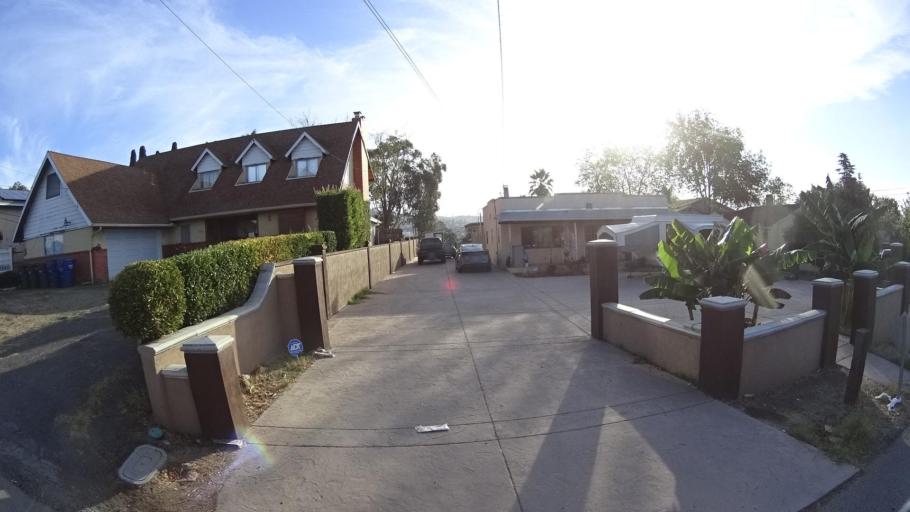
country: US
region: California
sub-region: San Diego County
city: La Presa
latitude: 32.7167
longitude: -117.0095
